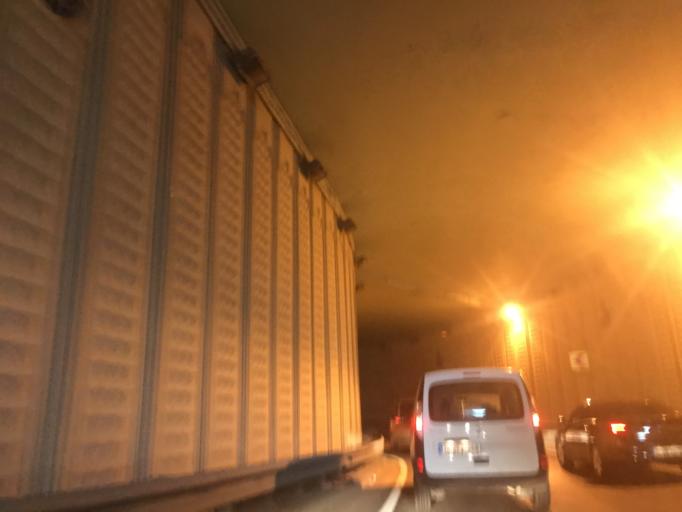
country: TR
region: Istanbul
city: Sisli
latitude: 41.0986
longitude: 29.0069
